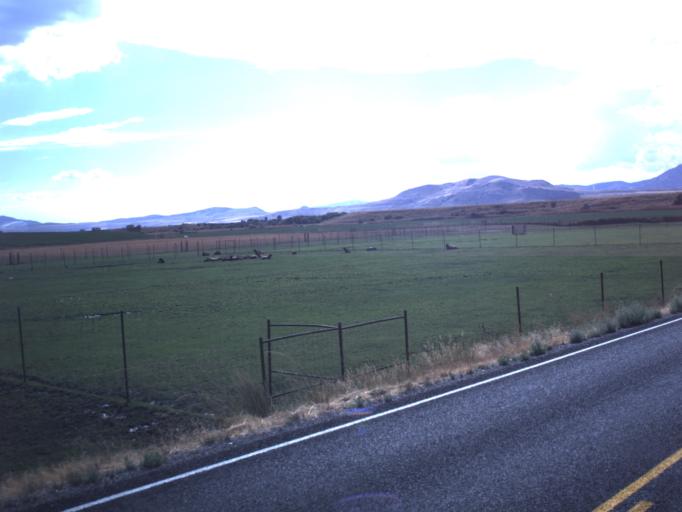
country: US
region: Utah
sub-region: Cache County
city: Richmond
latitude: 41.9238
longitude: -111.8432
